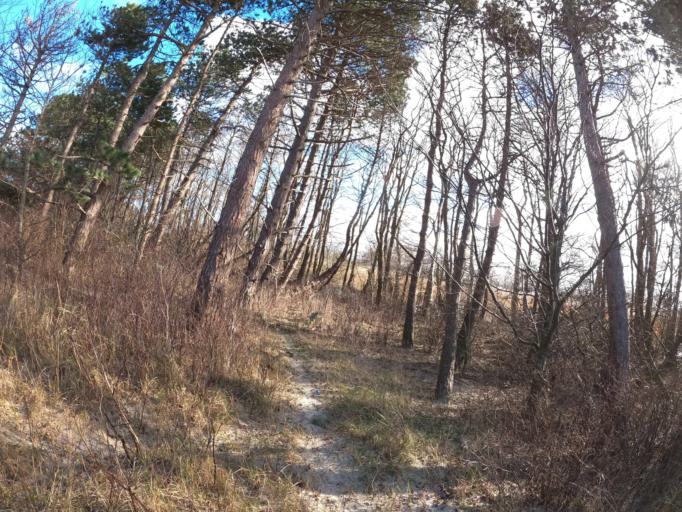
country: PL
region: West Pomeranian Voivodeship
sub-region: Powiat koszalinski
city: Sianow
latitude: 54.3260
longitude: 16.2244
